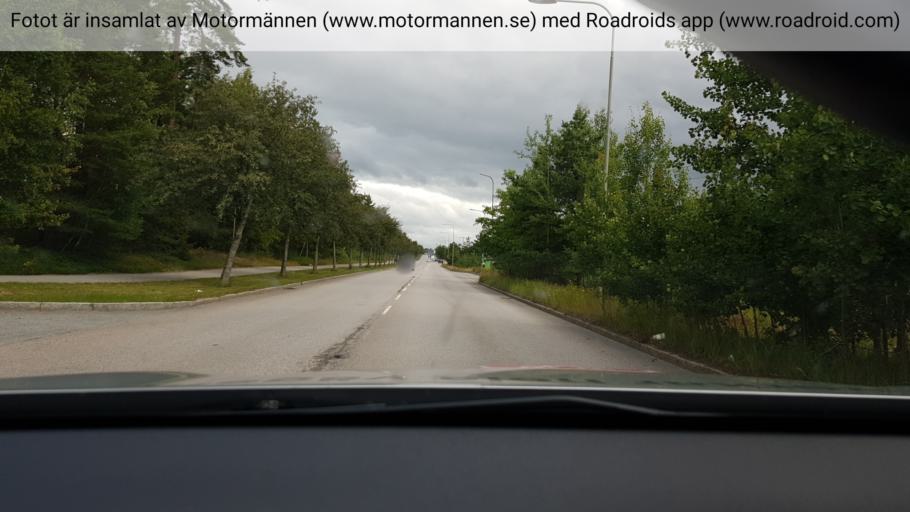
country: SE
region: Stockholm
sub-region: Nacka Kommun
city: Alta
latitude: 59.2345
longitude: 18.1944
